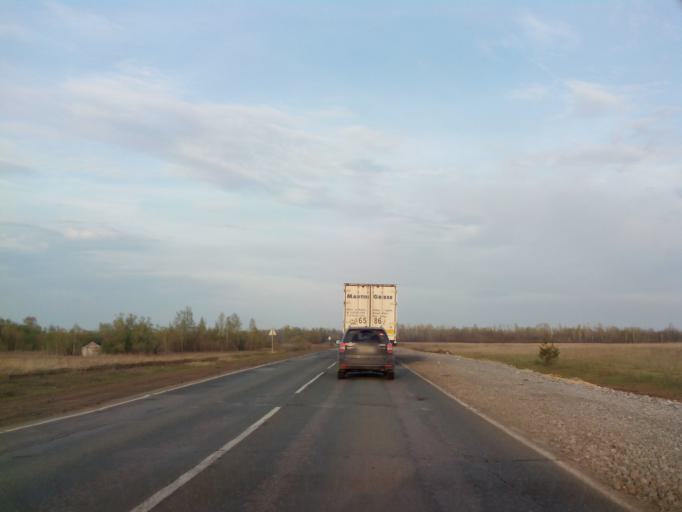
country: RU
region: Rjazan
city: Zarechnyy
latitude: 53.7522
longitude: 39.8214
